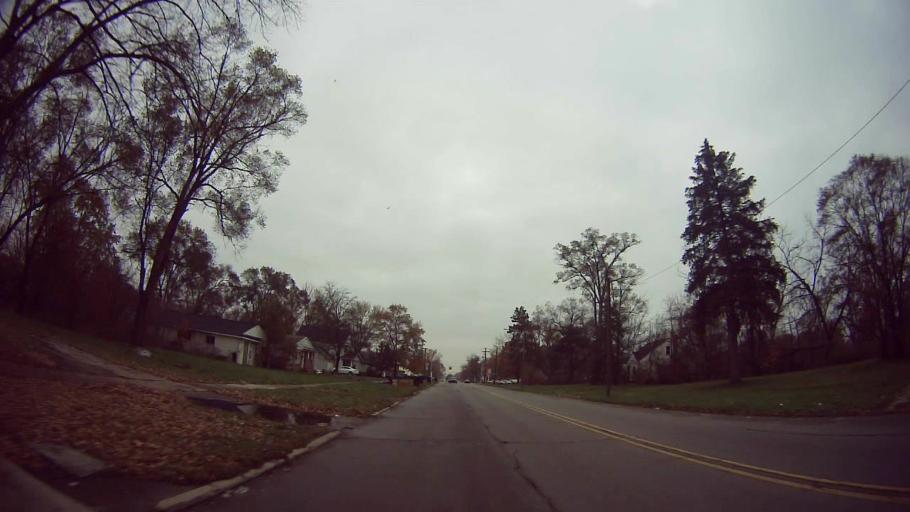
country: US
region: Michigan
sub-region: Wayne County
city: Redford
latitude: 42.4019
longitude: -83.2568
